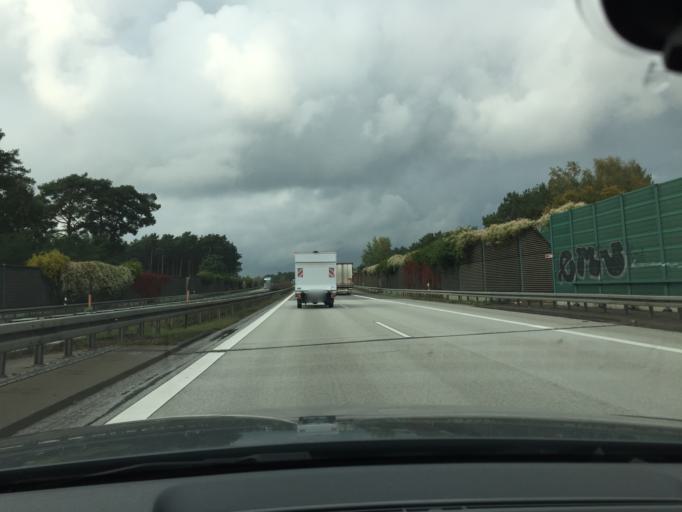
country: DE
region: Brandenburg
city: Schwerin
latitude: 52.1622
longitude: 13.6445
